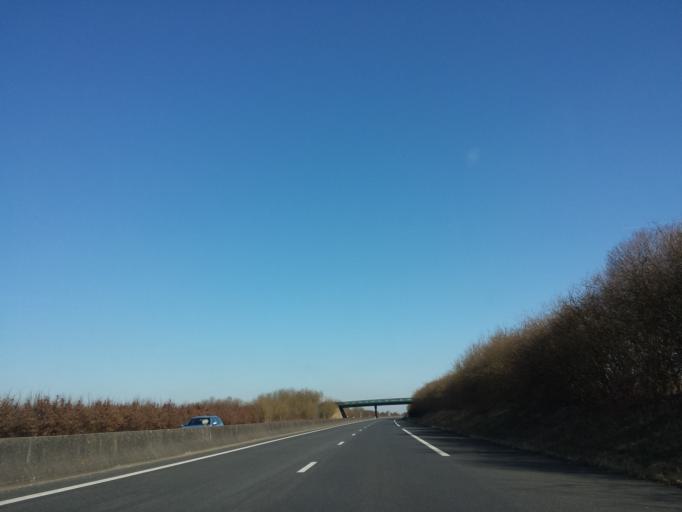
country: FR
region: Picardie
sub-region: Departement de l'Oise
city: Tille
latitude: 49.4989
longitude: 2.1712
